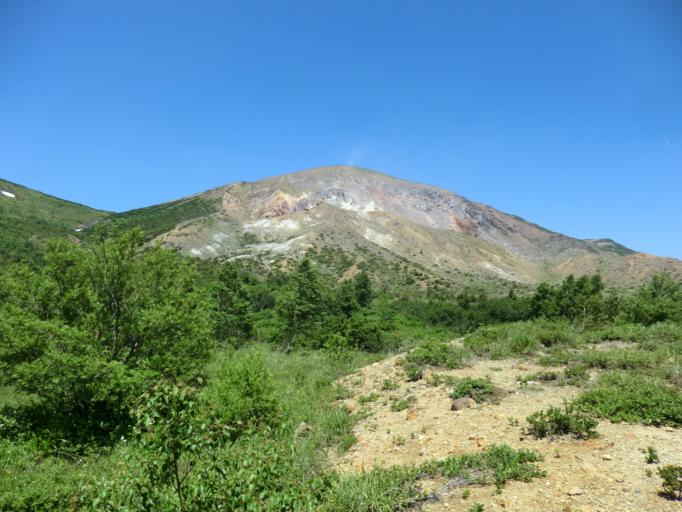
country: JP
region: Fukushima
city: Inawashiro
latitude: 37.7198
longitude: 140.2524
